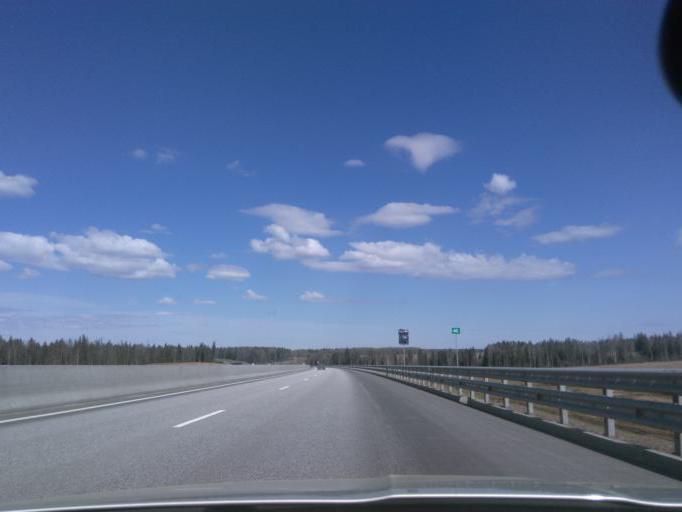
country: RU
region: Moskovskaya
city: Mendeleyevo
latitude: 56.0831
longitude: 37.2079
